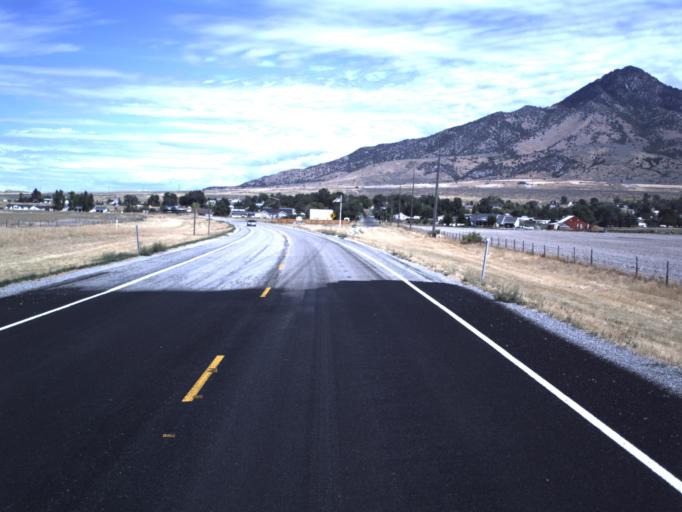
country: US
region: Utah
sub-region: Box Elder County
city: Garland
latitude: 41.8672
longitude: -112.1468
